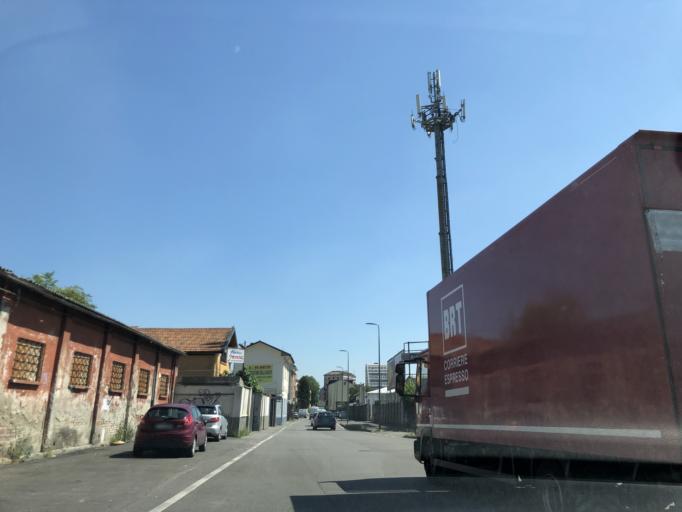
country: IT
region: Lombardy
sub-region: Citta metropolitana di Milano
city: Cormano
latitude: 45.5113
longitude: 9.1667
